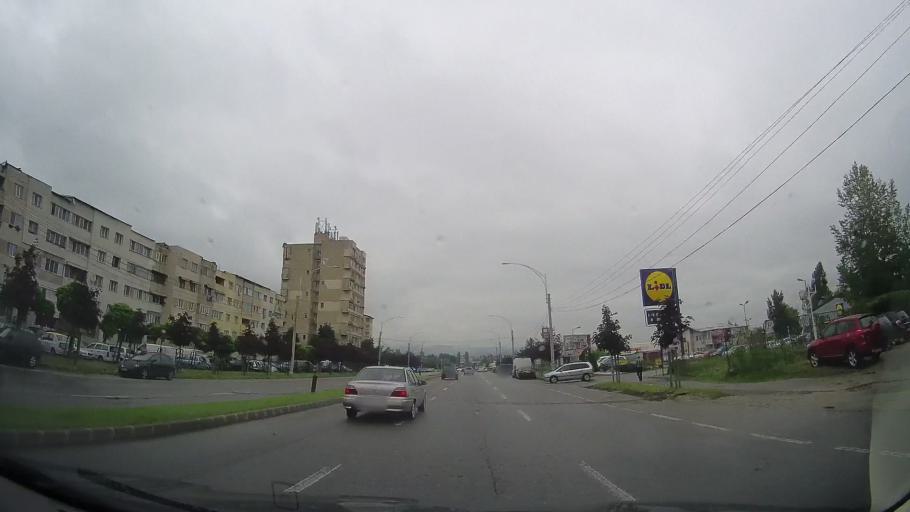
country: RO
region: Mehedinti
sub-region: Municipiul Drobeta-Turnu Severin
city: Drobeta-Turnu Severin
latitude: 44.6324
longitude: 22.6766
